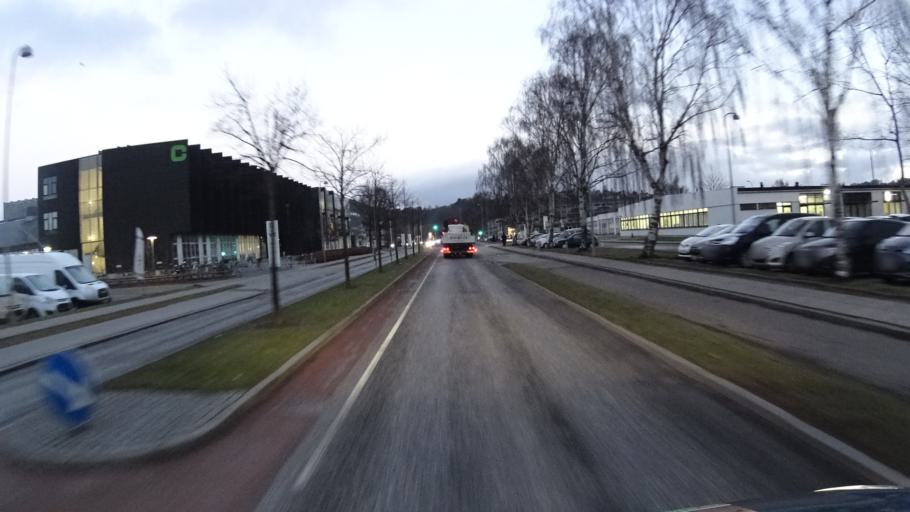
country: DK
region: South Denmark
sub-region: Vejle Kommune
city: Vejle
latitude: 55.7090
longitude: 9.5230
